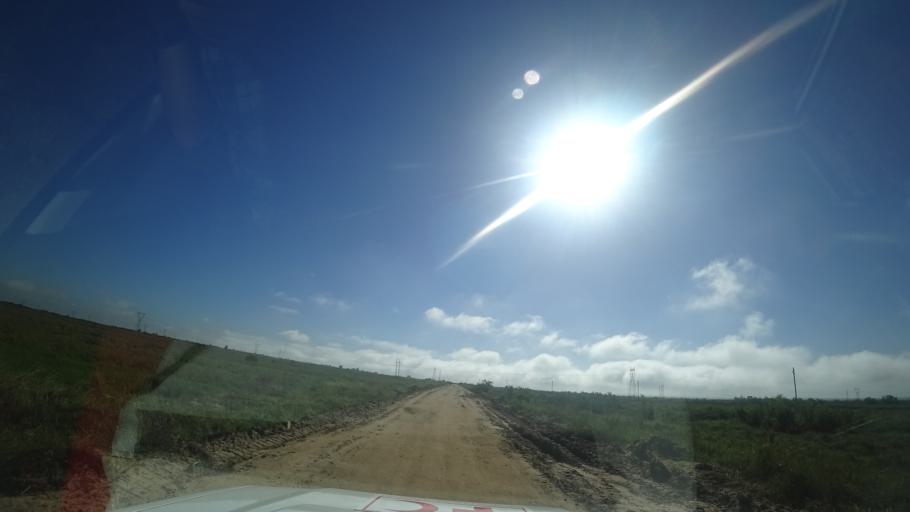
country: MZ
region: Sofala
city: Dondo
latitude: -19.4656
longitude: 34.5602
